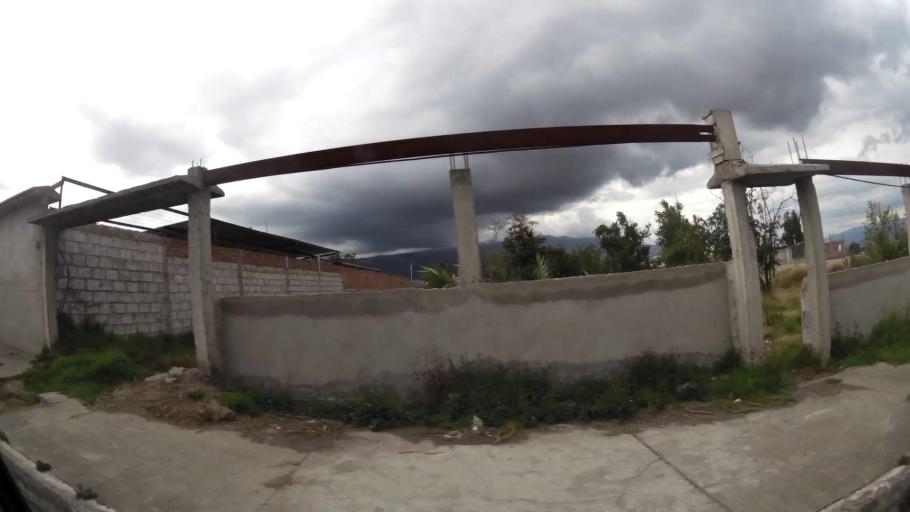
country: EC
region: Tungurahua
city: Ambato
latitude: -1.2680
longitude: -78.6199
